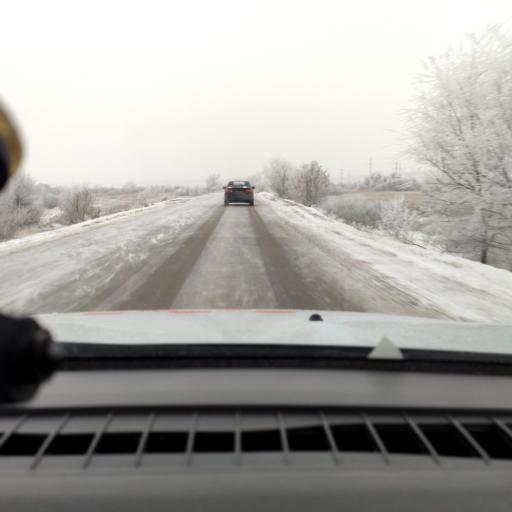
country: RU
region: Samara
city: Samara
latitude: 53.1013
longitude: 50.2282
